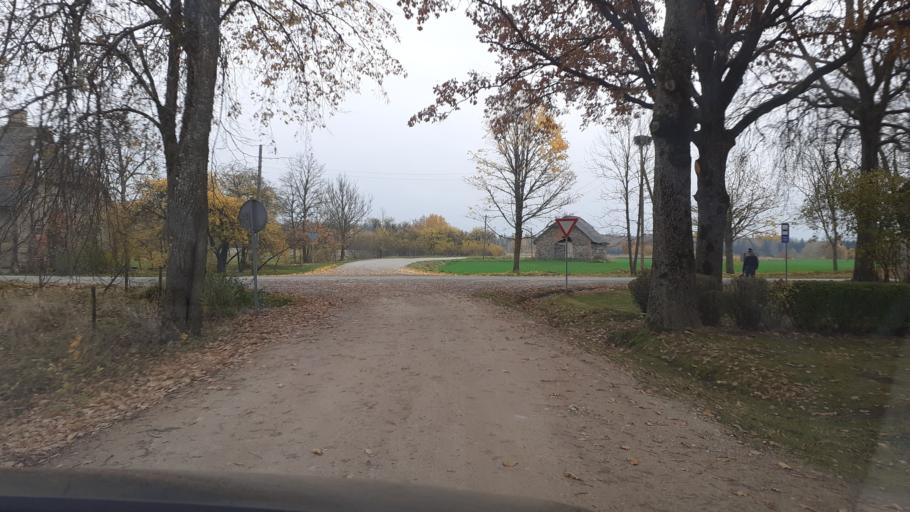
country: LV
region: Skrunda
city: Skrunda
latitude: 56.8574
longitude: 22.2305
